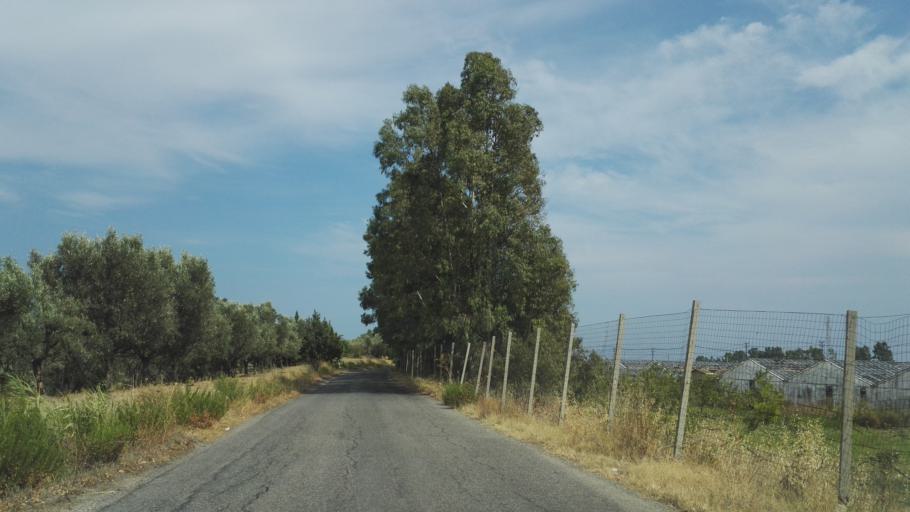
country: IT
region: Calabria
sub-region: Provincia di Reggio Calabria
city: Monasterace Marina
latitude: 38.4272
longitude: 16.5602
